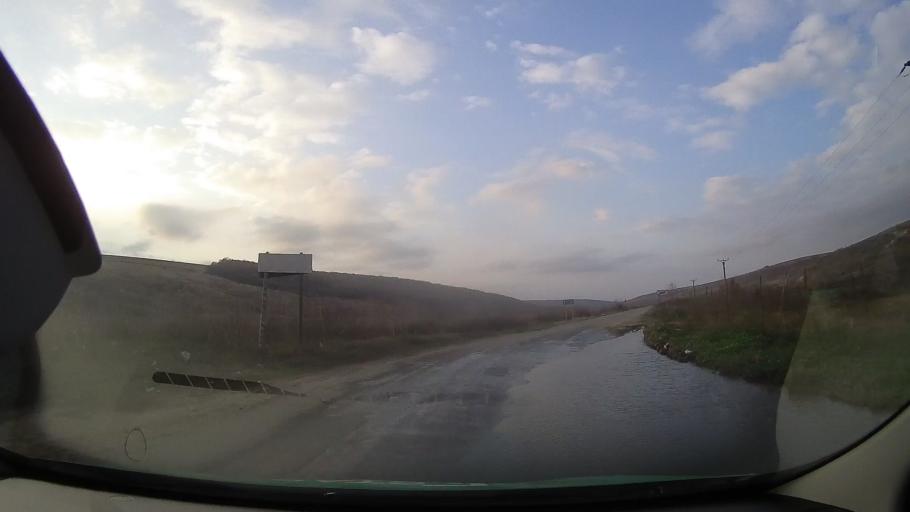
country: RO
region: Constanta
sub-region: Comuna Dobromir
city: Dobromir
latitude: 44.0218
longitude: 27.8709
